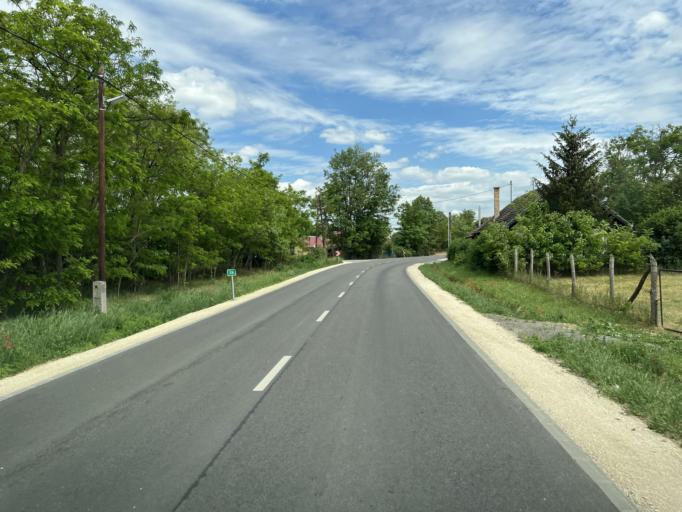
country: HU
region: Pest
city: Koka
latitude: 47.4748
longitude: 19.5643
